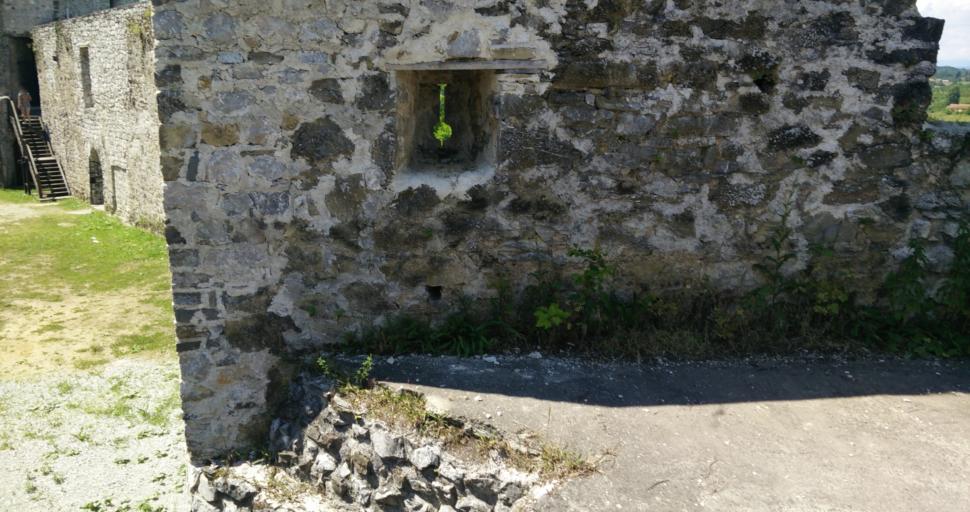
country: HR
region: Karlovacka
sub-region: Grad Karlovac
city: Karlovac
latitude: 45.4826
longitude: 15.4529
